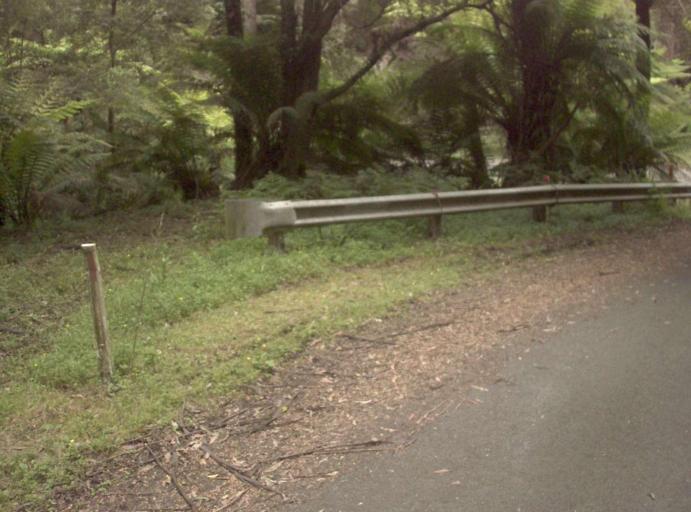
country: AU
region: Victoria
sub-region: Latrobe
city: Traralgon
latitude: -38.4477
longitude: 146.5341
